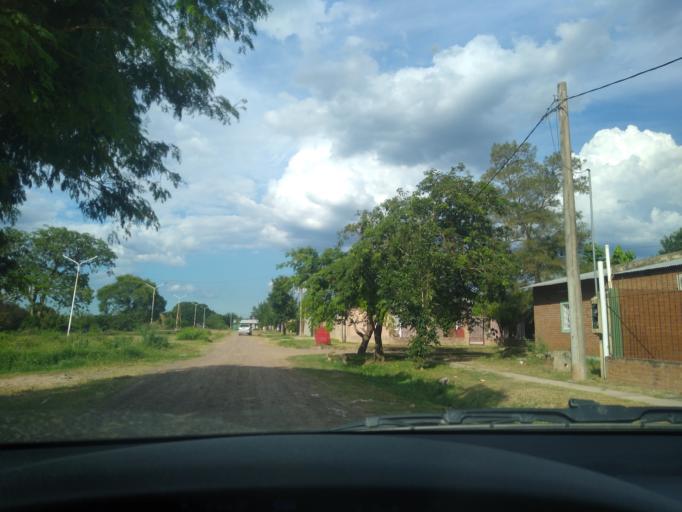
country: AR
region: Chaco
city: Fontana
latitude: -27.4059
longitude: -59.0488
